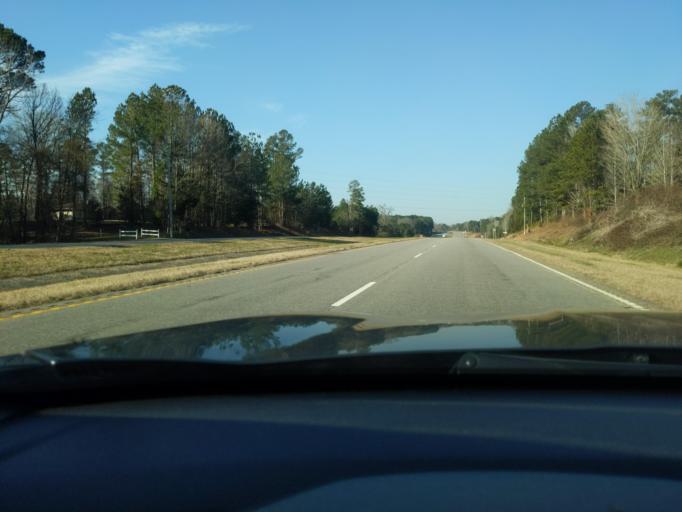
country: US
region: South Carolina
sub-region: Greenwood County
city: Greenwood
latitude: 34.1895
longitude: -82.2623
